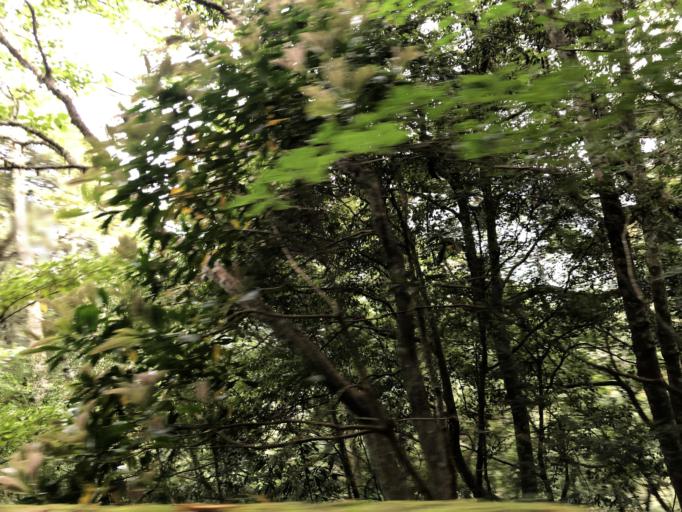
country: TW
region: Taiwan
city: Daxi
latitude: 24.7050
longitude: 121.4244
